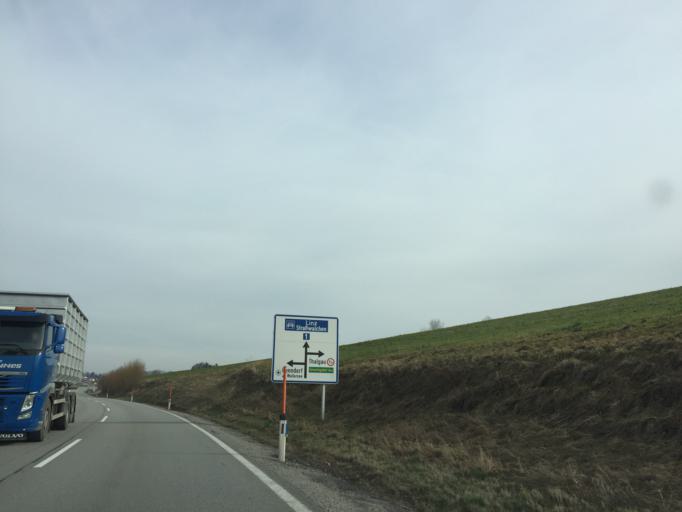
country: AT
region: Salzburg
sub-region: Politischer Bezirk Salzburg-Umgebung
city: Henndorf am Wallersee
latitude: 47.8842
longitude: 13.1749
